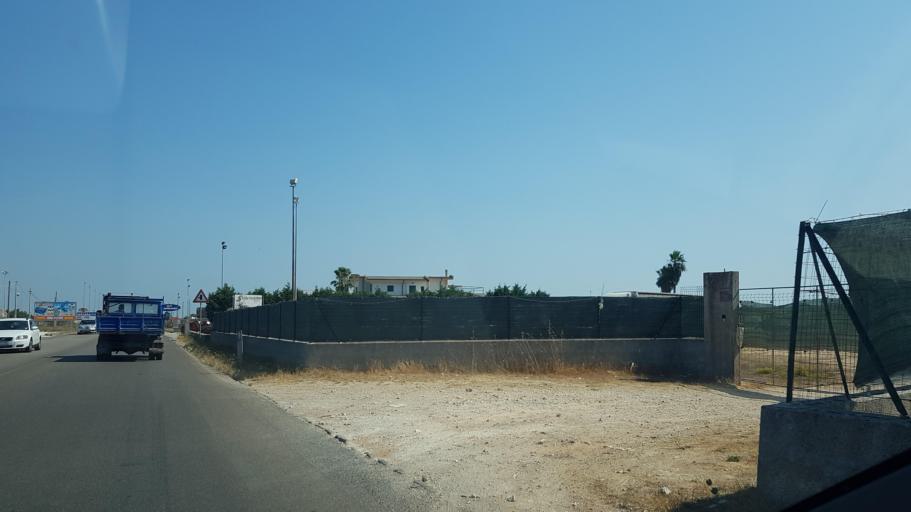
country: IT
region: Apulia
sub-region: Provincia di Lecce
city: Nociglia
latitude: 40.0114
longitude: 18.3241
